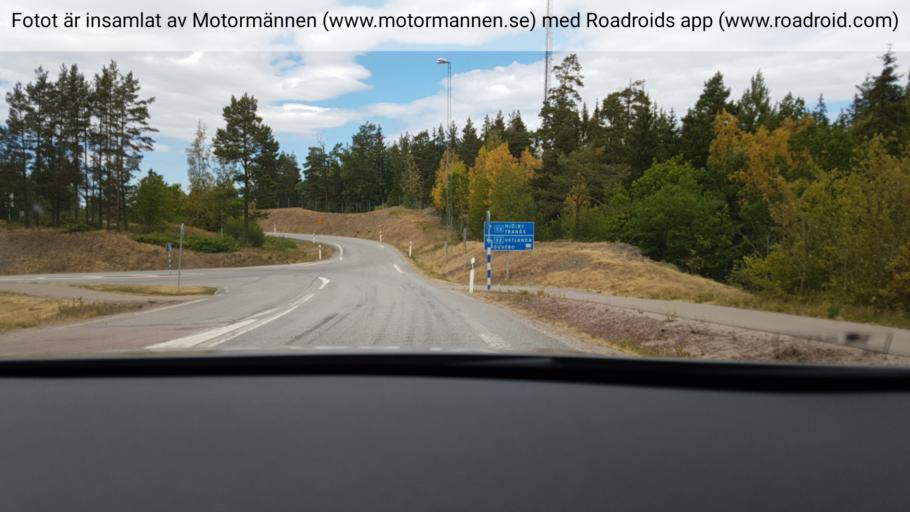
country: SE
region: Joenkoeping
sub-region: Tranas Kommun
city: Tranas
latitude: 58.0331
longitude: 14.9519
